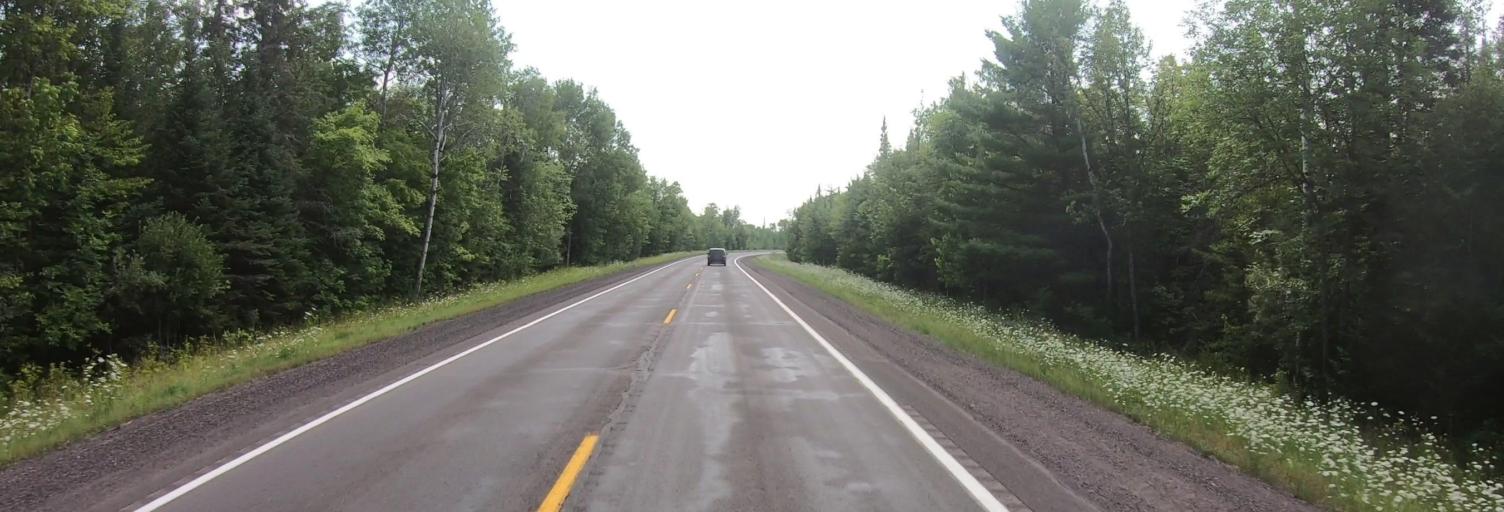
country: US
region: Michigan
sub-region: Ontonagon County
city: Ontonagon
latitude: 46.7383
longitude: -89.1115
